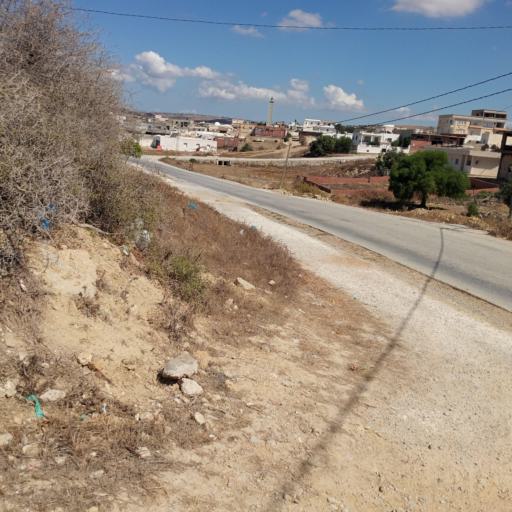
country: TN
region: Nabul
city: Qulaybiyah
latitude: 36.8582
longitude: 11.0325
